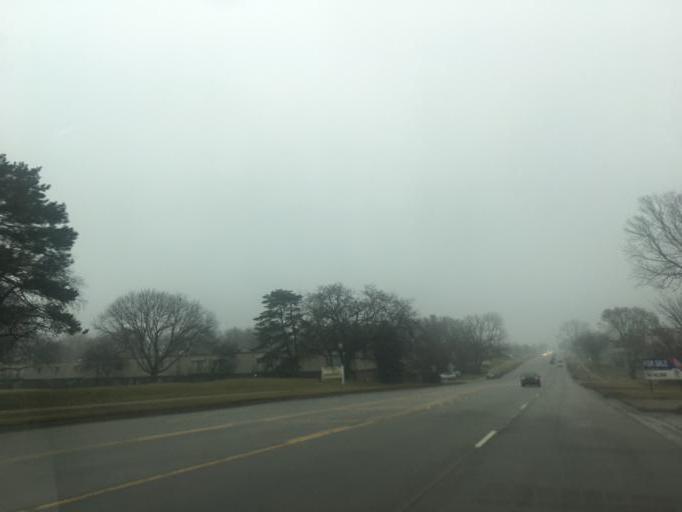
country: US
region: Illinois
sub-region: DuPage County
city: Lisle
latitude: 41.7969
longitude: -88.1053
